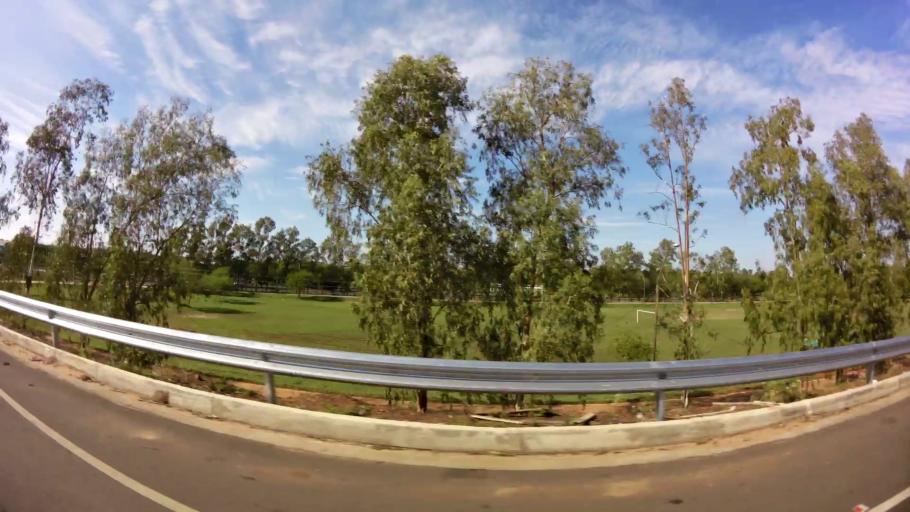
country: PY
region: Central
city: Fernando de la Mora
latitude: -25.2617
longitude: -57.5219
